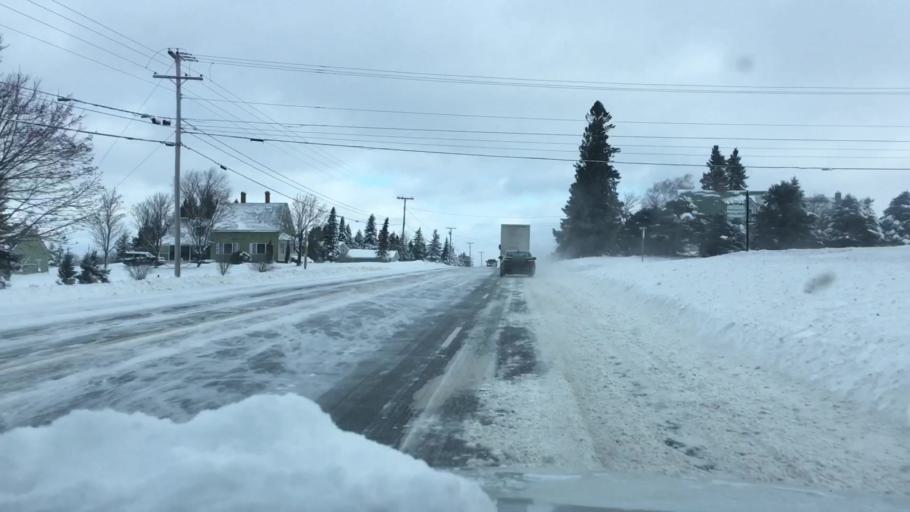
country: US
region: Maine
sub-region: Aroostook County
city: Presque Isle
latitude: 46.7276
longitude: -68.0033
